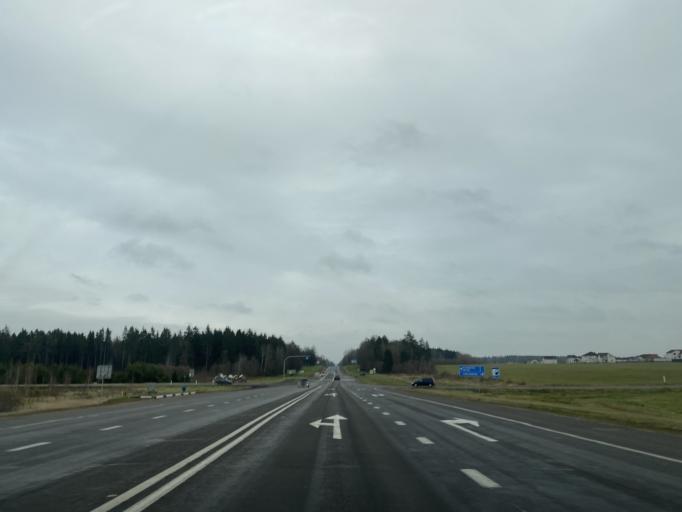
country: BY
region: Minsk
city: Horad Smalyavichy
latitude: 54.0497
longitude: 28.0838
